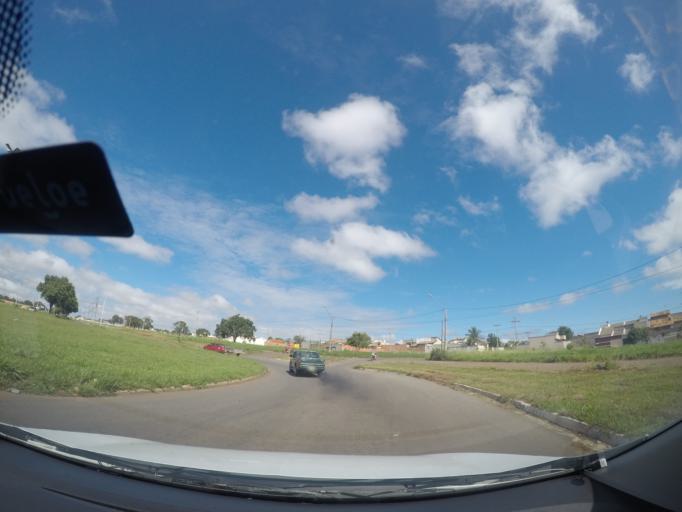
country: BR
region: Goias
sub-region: Goiania
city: Goiania
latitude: -16.6521
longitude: -49.1727
